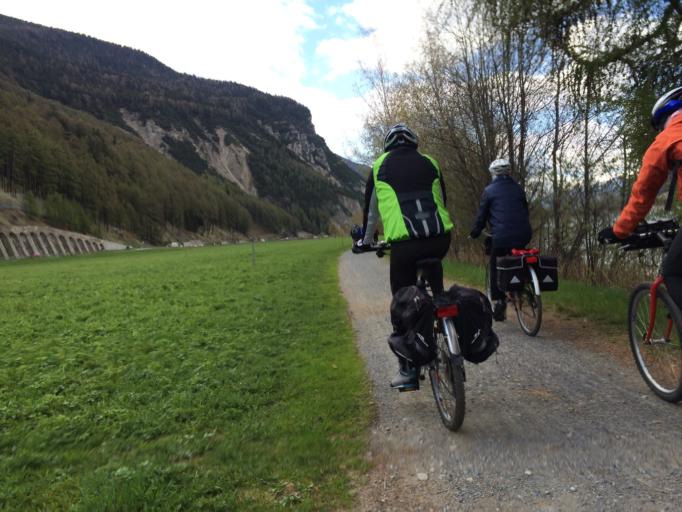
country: IT
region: Trentino-Alto Adige
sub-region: Bolzano
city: Curon Venosta
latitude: 46.8027
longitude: 10.5381
